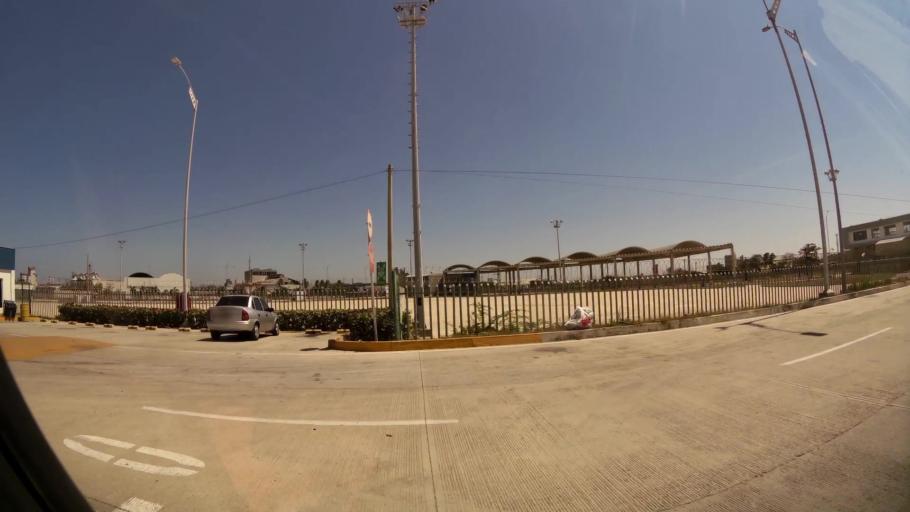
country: CO
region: Atlantico
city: Barranquilla
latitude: 10.9862
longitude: -74.7722
